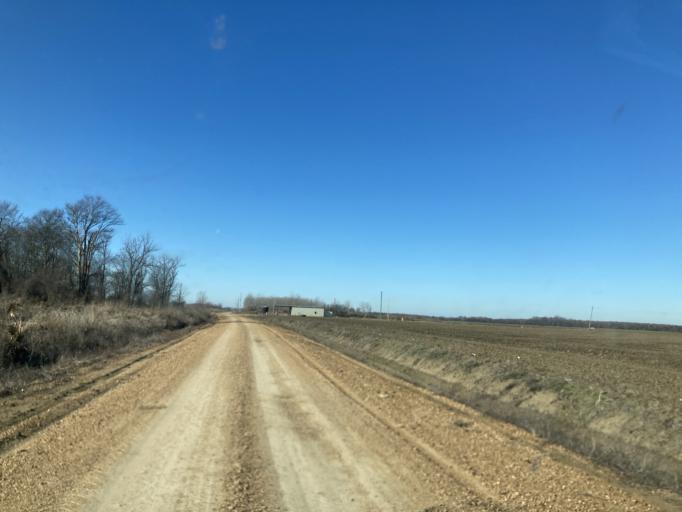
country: US
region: Mississippi
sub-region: Humphreys County
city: Belzoni
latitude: 32.9811
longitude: -90.6200
